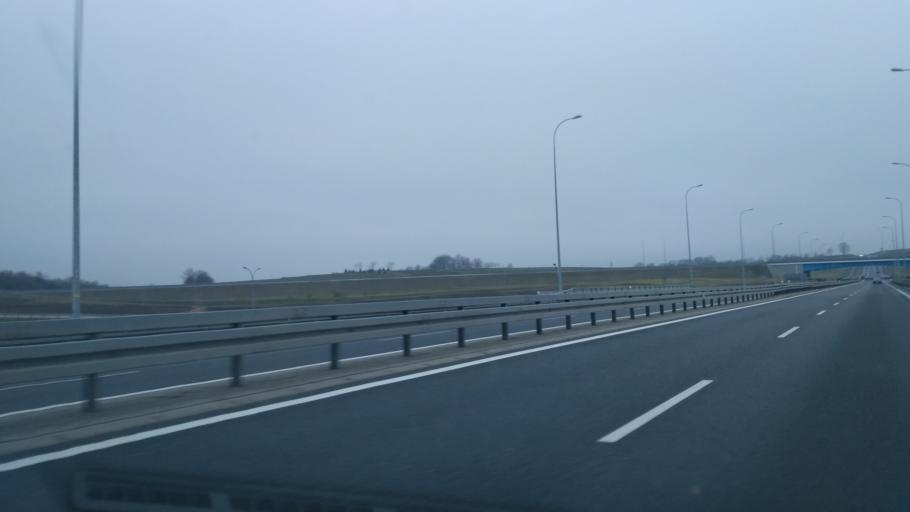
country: PL
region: Subcarpathian Voivodeship
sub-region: Powiat przeworski
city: Mirocin
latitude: 50.0371
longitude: 22.5782
